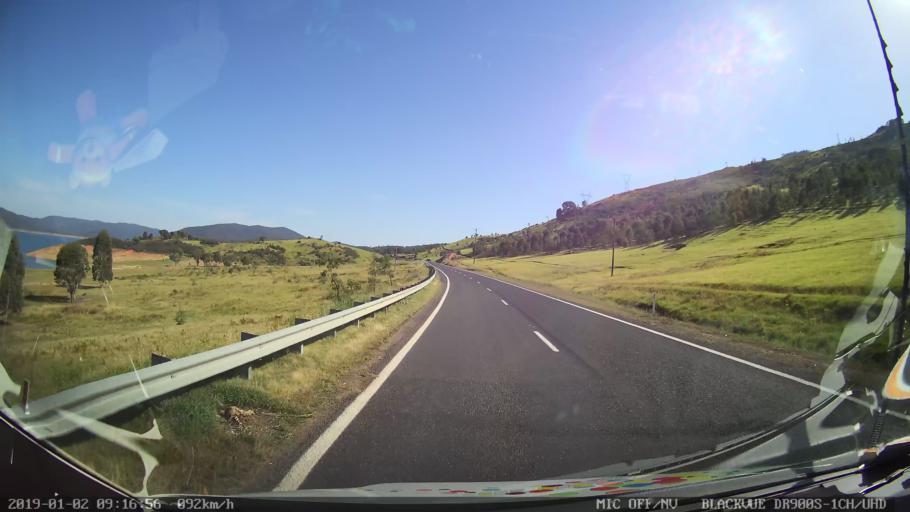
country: AU
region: New South Wales
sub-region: Tumut Shire
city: Tumut
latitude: -35.4475
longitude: 148.2858
